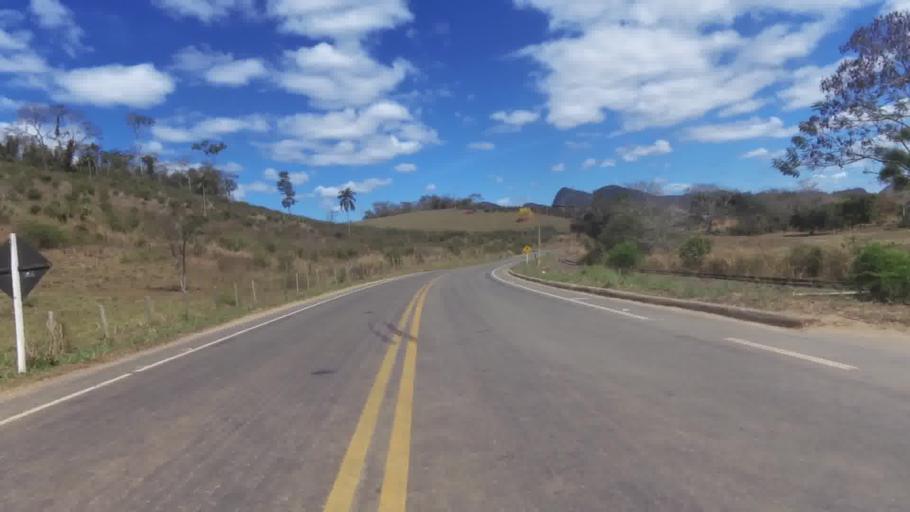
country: BR
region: Espirito Santo
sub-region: Cachoeiro De Itapemirim
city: Cachoeiro de Itapemirim
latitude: -20.9125
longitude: -41.2100
